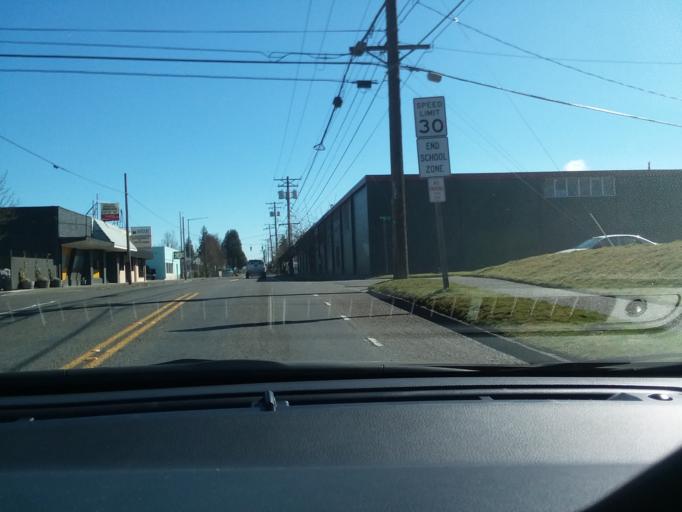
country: US
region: Washington
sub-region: Pierce County
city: Tacoma
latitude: 47.2500
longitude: -122.4751
